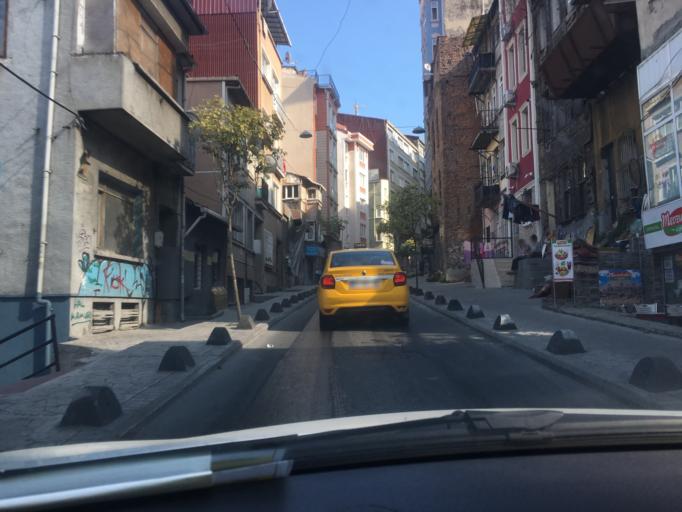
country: TR
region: Istanbul
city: Eminoenue
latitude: 41.0379
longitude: 28.9747
